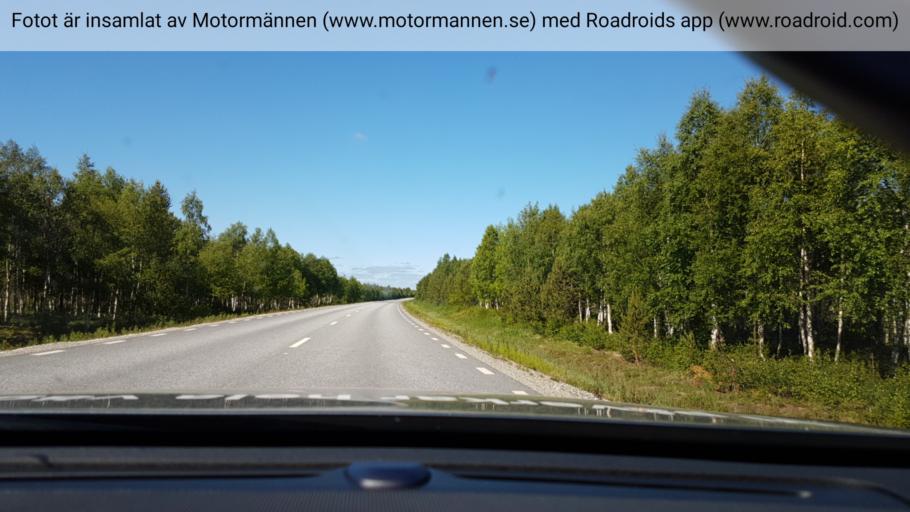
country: SE
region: Vaesterbotten
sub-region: Asele Kommun
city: Insjon
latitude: 64.1973
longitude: 17.5999
